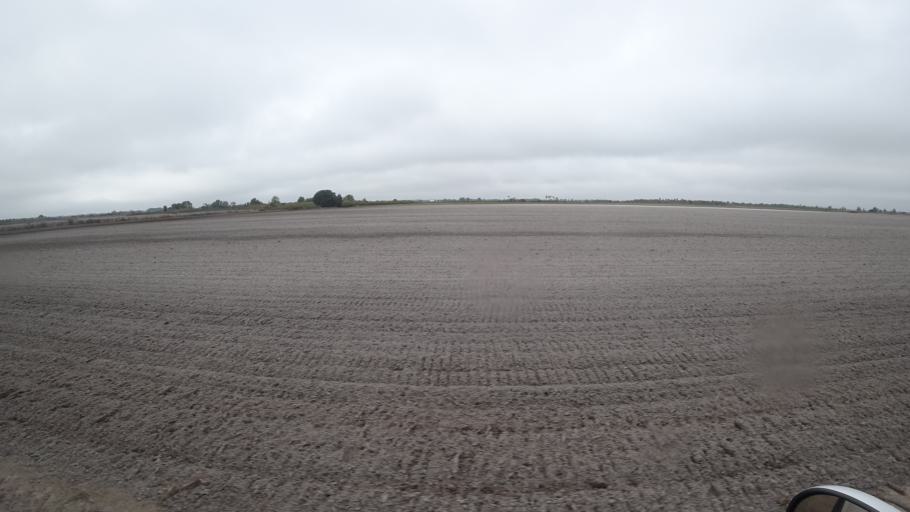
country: US
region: Florida
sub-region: Sarasota County
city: Warm Mineral Springs
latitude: 27.2860
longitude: -82.1754
